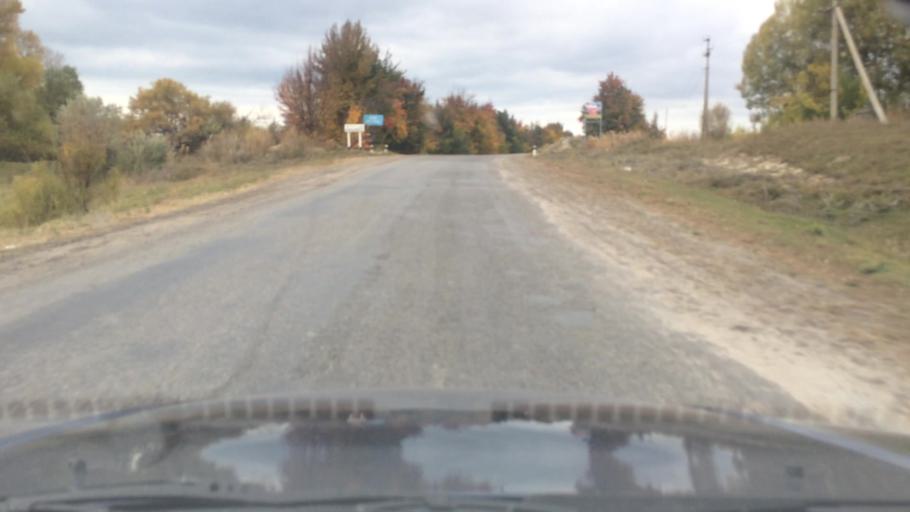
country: KG
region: Ysyk-Koel
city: Tyup
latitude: 42.7663
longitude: 78.1813
